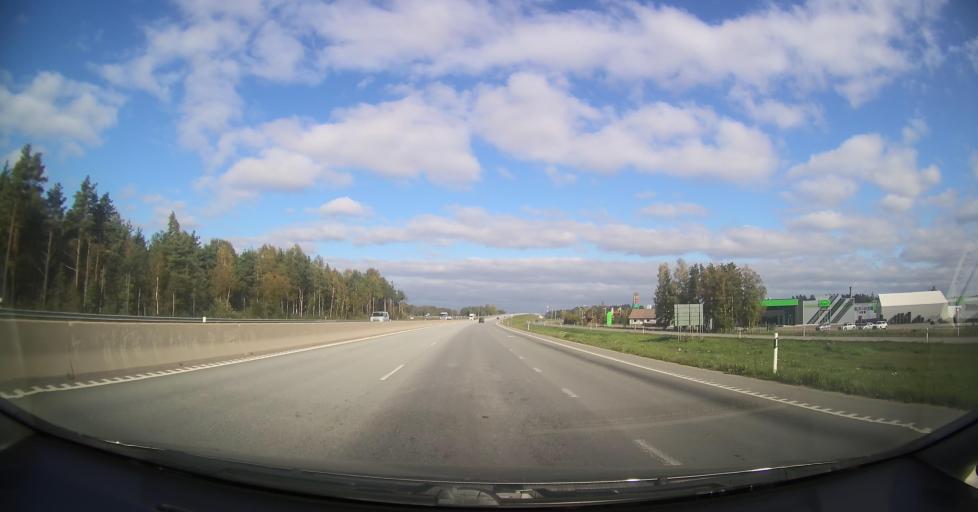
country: EE
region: Harju
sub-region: Rae vald
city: Jueri
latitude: 59.3982
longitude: 24.9156
